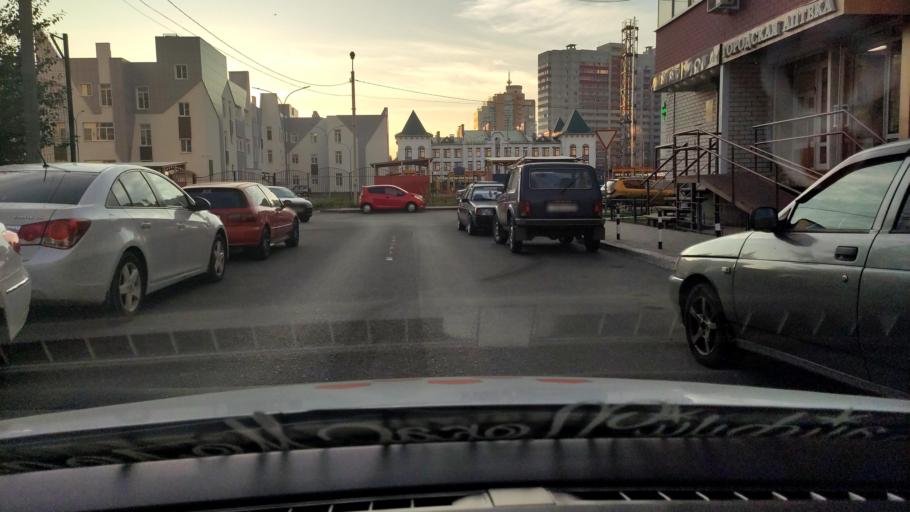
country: RU
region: Voronezj
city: Voronezh
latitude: 51.7111
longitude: 39.2006
